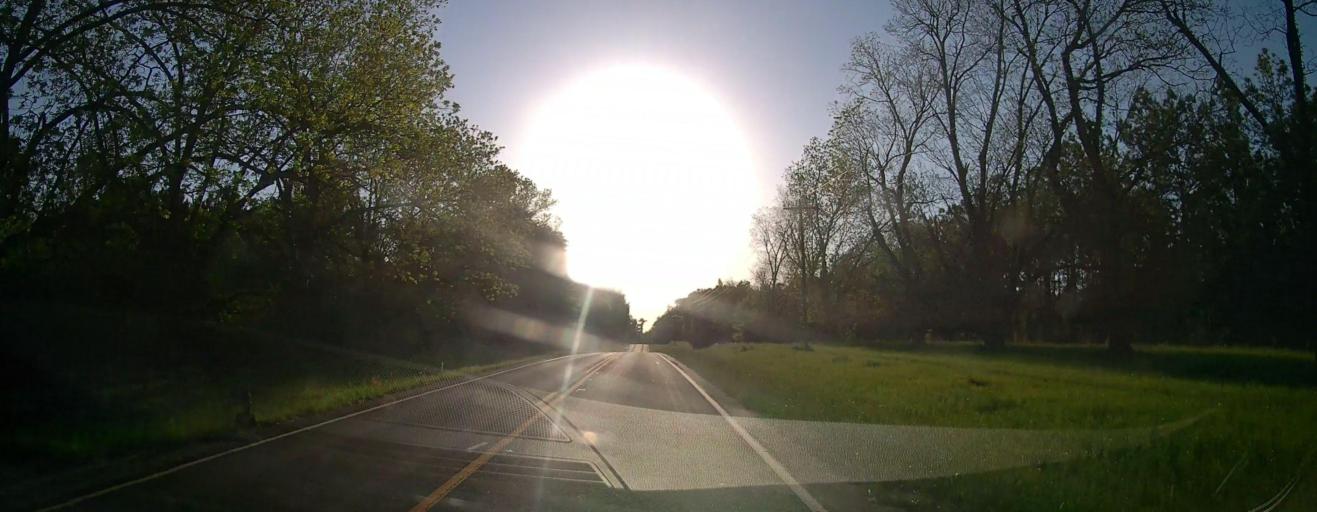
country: US
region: Georgia
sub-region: Macon County
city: Oglethorpe
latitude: 32.3199
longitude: -84.1962
